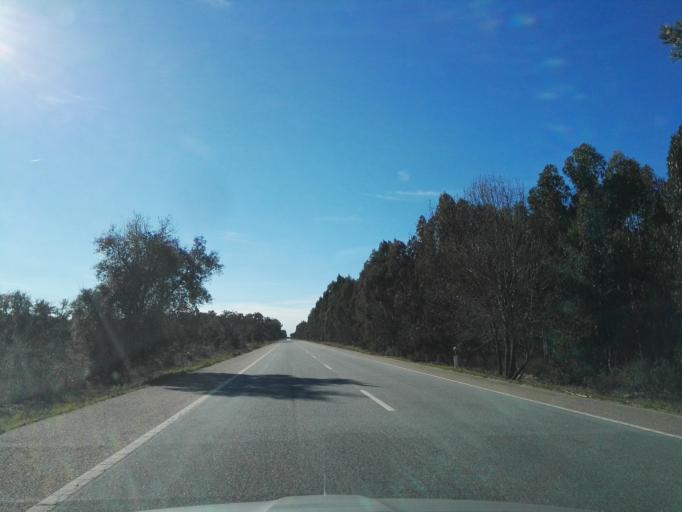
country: PT
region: Portalegre
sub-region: Gaviao
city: Gaviao
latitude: 39.4456
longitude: -7.8221
